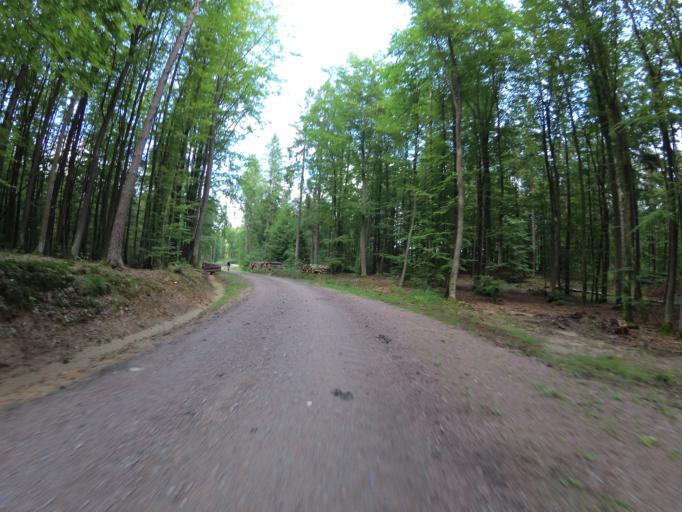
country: PL
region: Pomeranian Voivodeship
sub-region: Powiat wejherowski
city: Bojano
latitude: 54.5102
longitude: 18.4218
